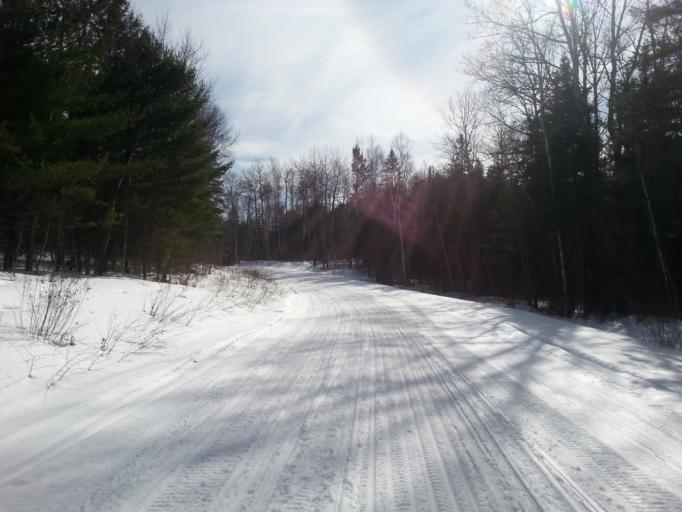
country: CA
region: Ontario
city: Greater Sudbury
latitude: 46.3420
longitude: -80.9025
